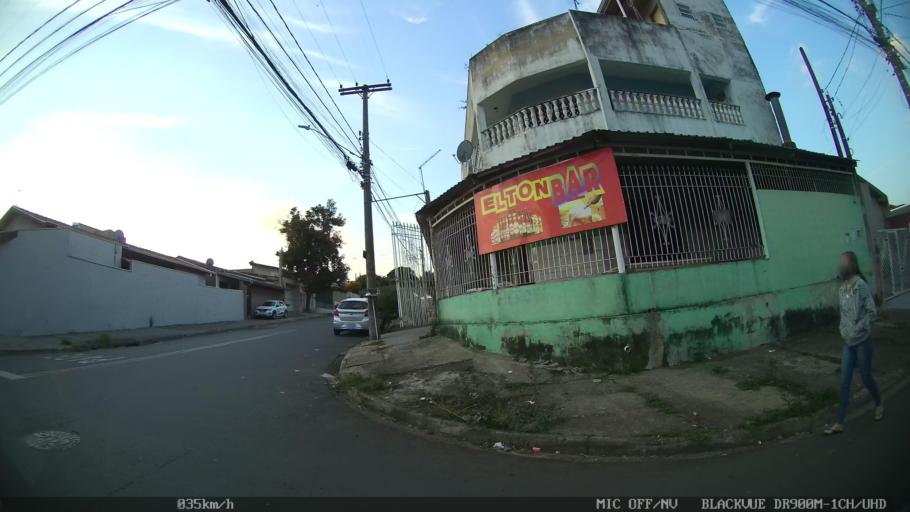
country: BR
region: Sao Paulo
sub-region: Hortolandia
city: Hortolandia
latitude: -22.8511
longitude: -47.2127
